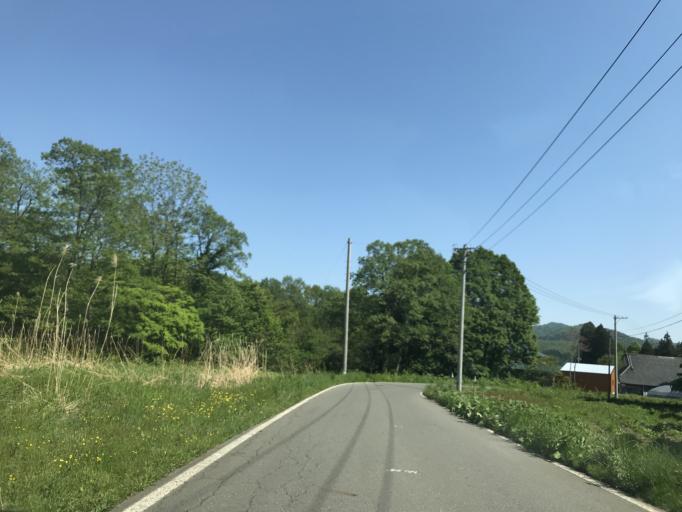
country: JP
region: Iwate
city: Shizukuishi
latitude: 39.5598
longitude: 140.8410
